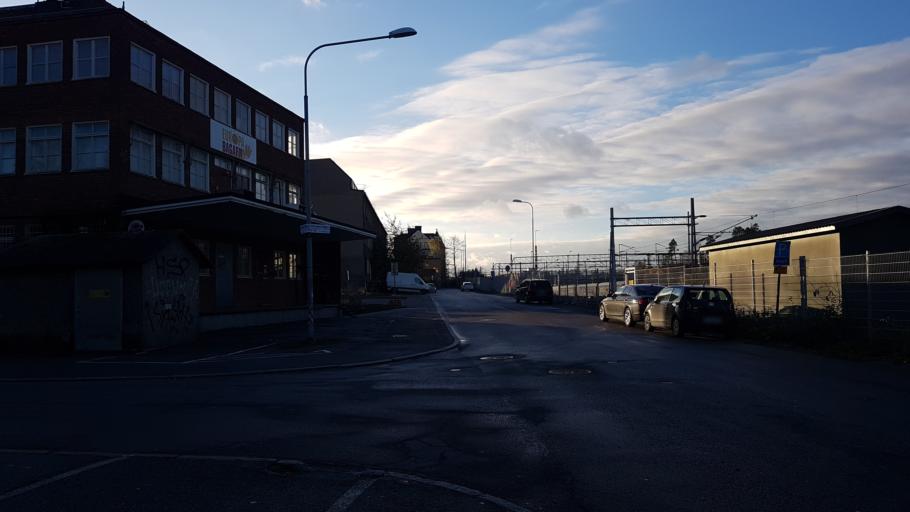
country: SE
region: Stockholm
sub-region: Solna Kommun
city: Solna
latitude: 59.3577
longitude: 18.0130
